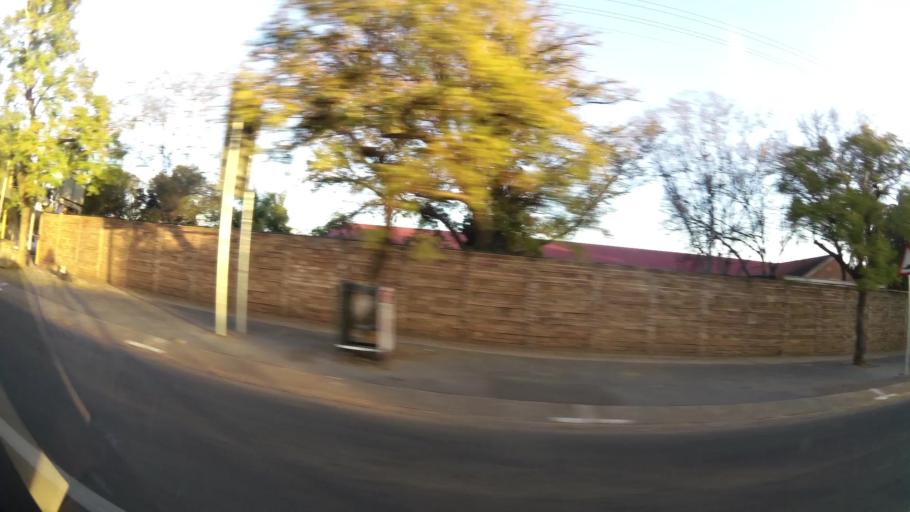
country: ZA
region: Gauteng
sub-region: City of Tshwane Metropolitan Municipality
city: Pretoria
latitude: -25.7115
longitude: 28.2360
